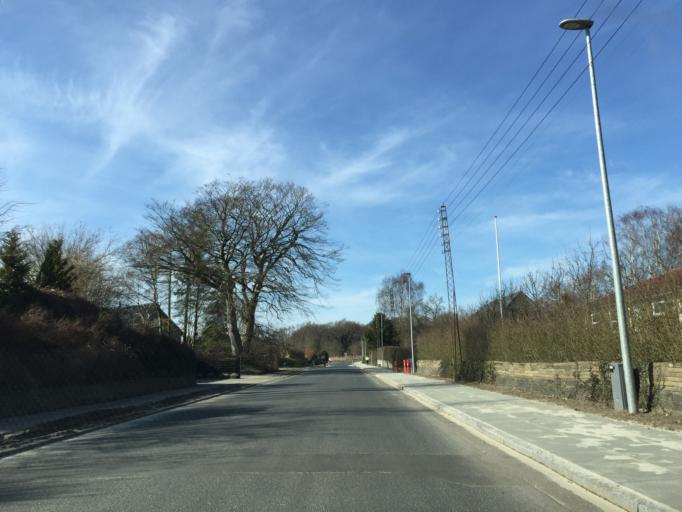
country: DK
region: Central Jutland
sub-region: Silkeborg Kommune
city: Silkeborg
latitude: 56.1941
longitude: 9.5349
